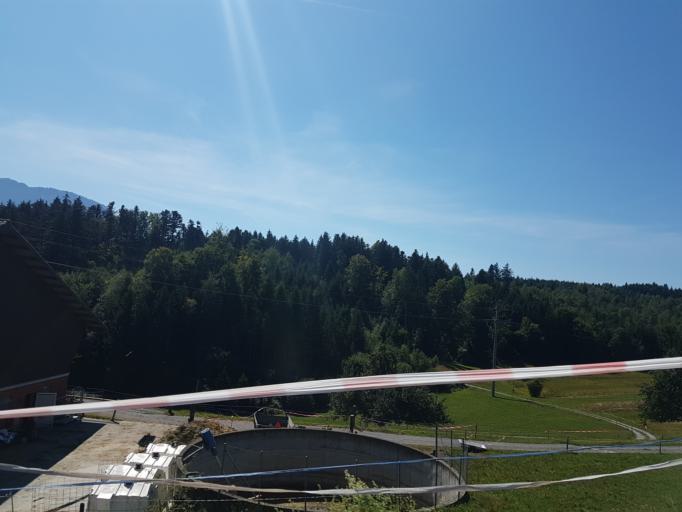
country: CH
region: Lucerne
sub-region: Lucerne-Land District
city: Udligenswil
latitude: 47.0876
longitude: 8.4072
